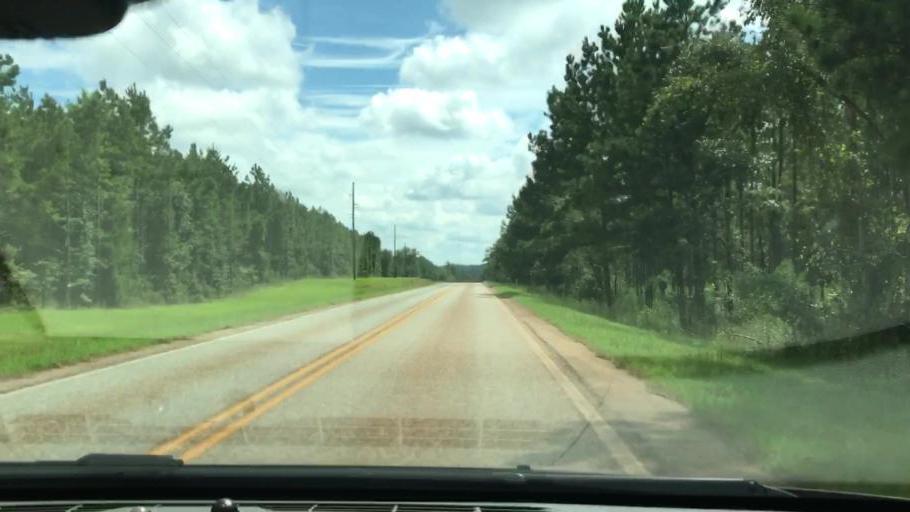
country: US
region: Georgia
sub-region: Stewart County
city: Lumpkin
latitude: 32.0621
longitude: -84.8300
